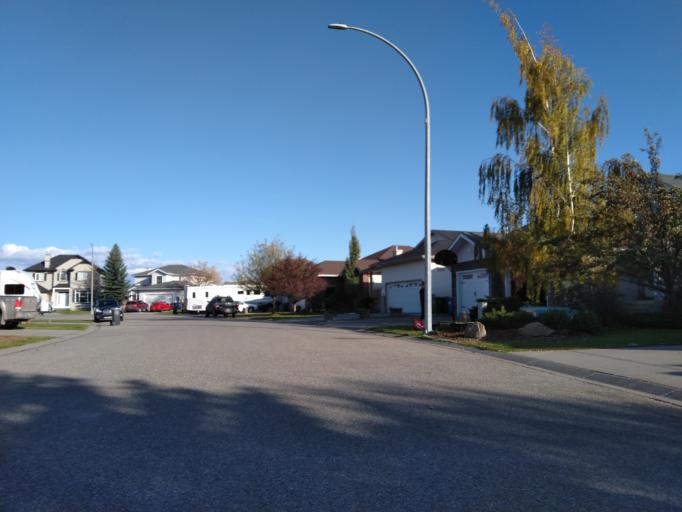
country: CA
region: Alberta
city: Cochrane
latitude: 51.1740
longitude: -114.4691
